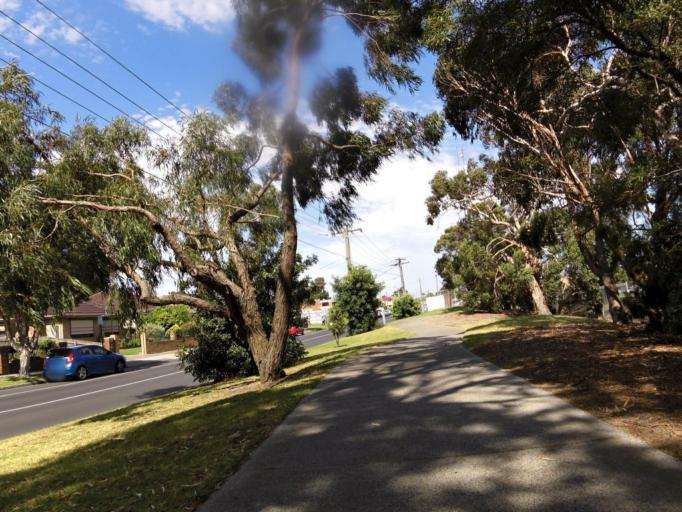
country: AU
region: Victoria
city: Clayton
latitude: -37.9224
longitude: 145.1178
